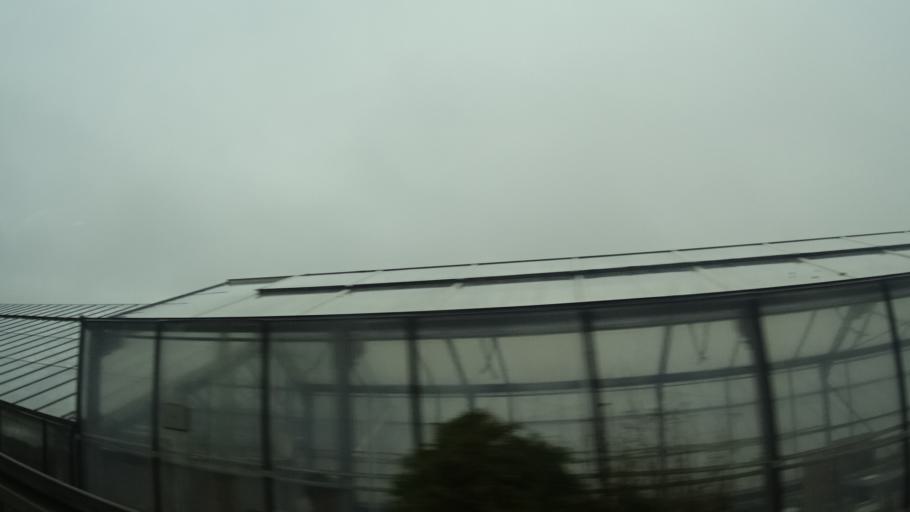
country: DE
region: Hesse
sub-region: Regierungsbezirk Kassel
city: Dipperz
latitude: 50.4844
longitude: 9.7951
